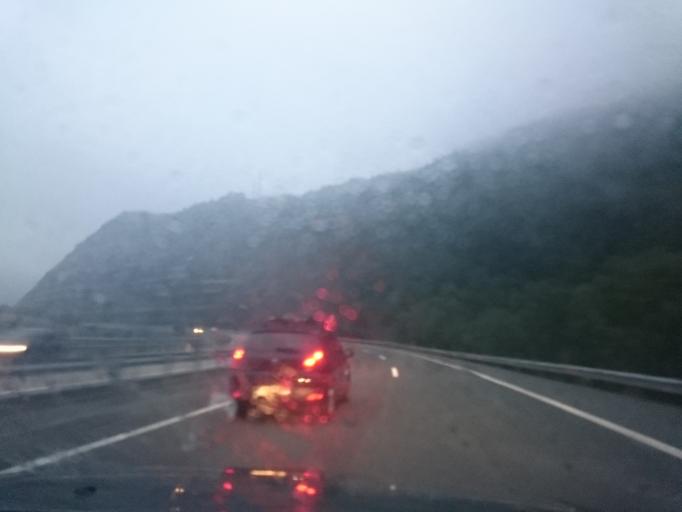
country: ES
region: Asturias
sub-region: Province of Asturias
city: Pola de Lena
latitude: 43.0302
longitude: -5.8190
